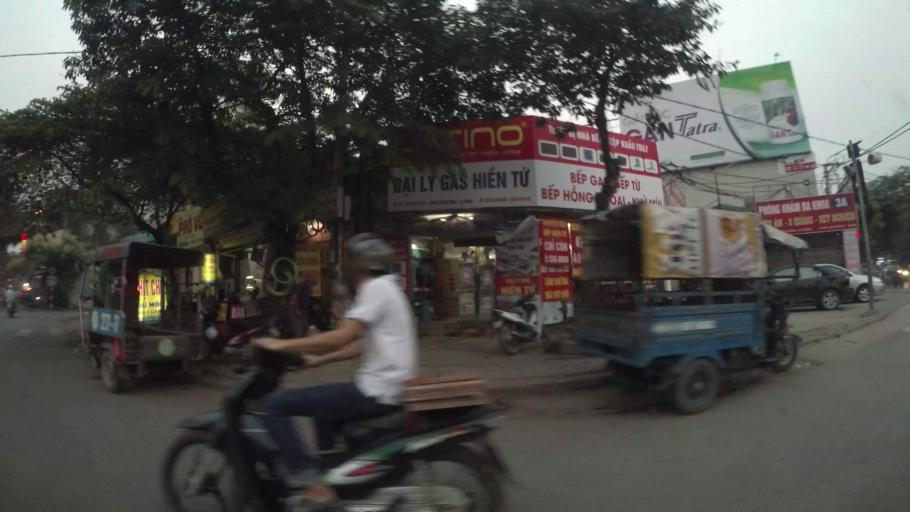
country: VN
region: Ha Noi
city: Ha Dong
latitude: 20.9719
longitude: 105.7832
